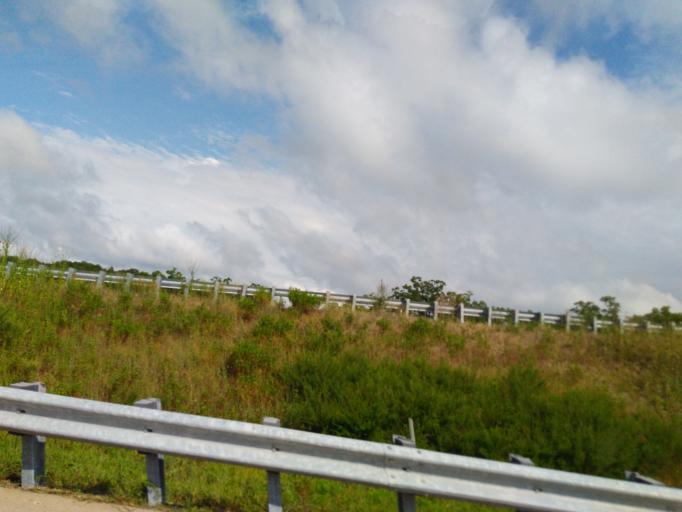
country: US
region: Missouri
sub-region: Jefferson County
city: Hillsboro
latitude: 38.3116
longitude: -90.5350
